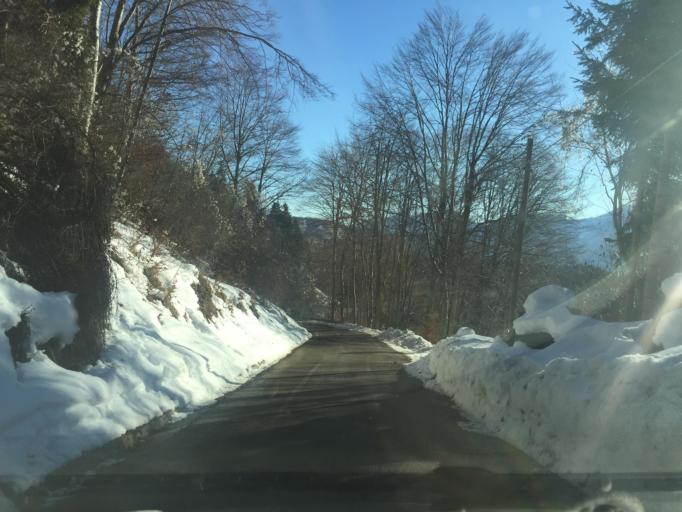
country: IT
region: Friuli Venezia Giulia
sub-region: Provincia di Udine
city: Lauco
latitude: 46.4467
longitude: 12.9326
